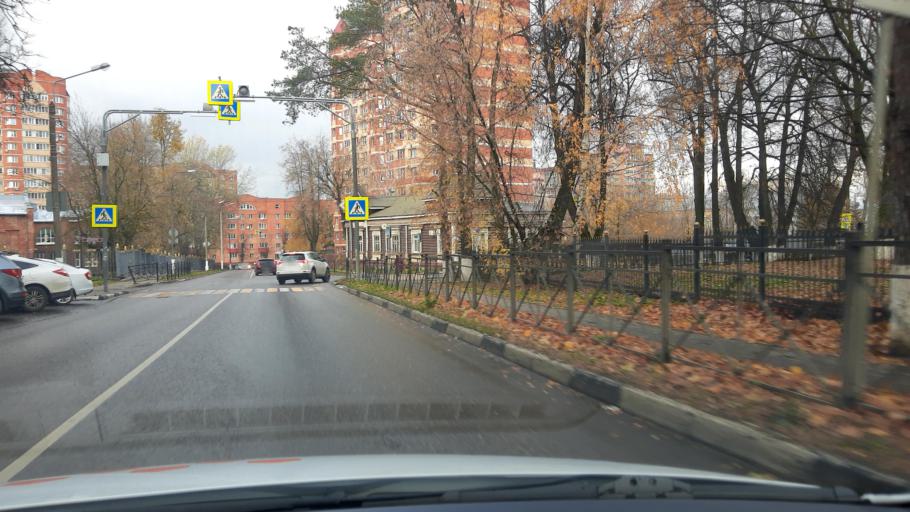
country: RU
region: Moskovskaya
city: Noginsk
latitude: 55.8506
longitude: 38.4314
